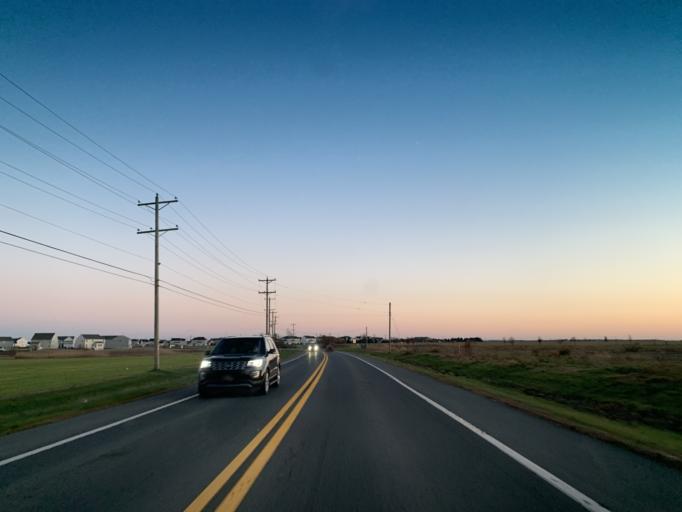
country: US
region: Delaware
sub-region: New Castle County
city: Middletown
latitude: 39.4321
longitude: -75.7429
